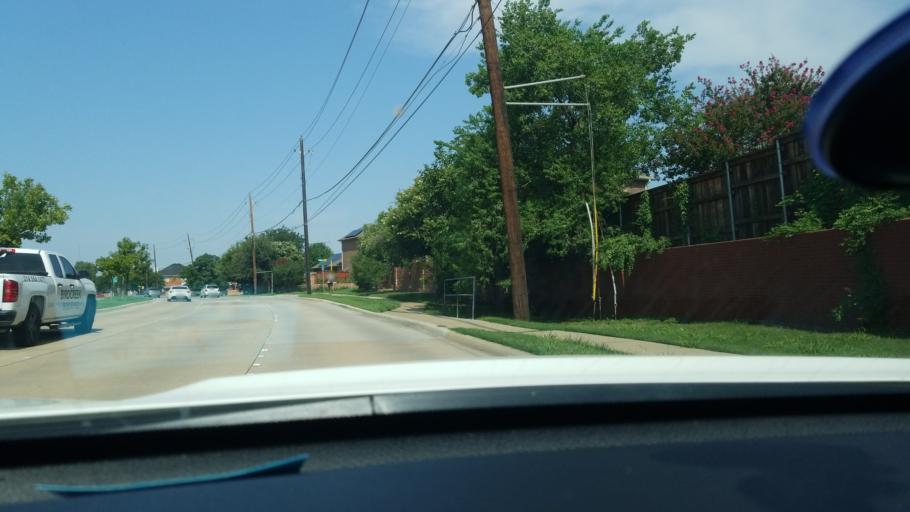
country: US
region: Texas
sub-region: Dallas County
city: Carrollton
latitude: 32.9710
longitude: -96.8713
